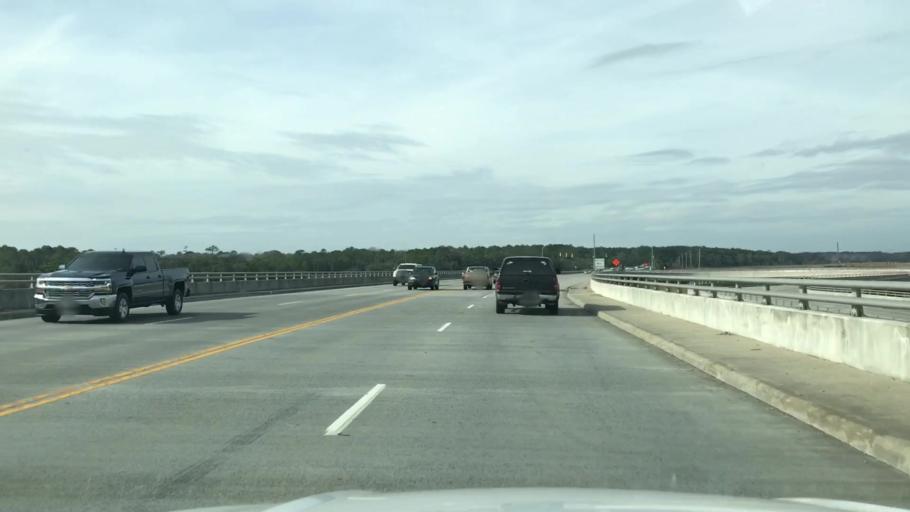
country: US
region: South Carolina
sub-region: Charleston County
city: Charleston
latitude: 32.7516
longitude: -80.0201
